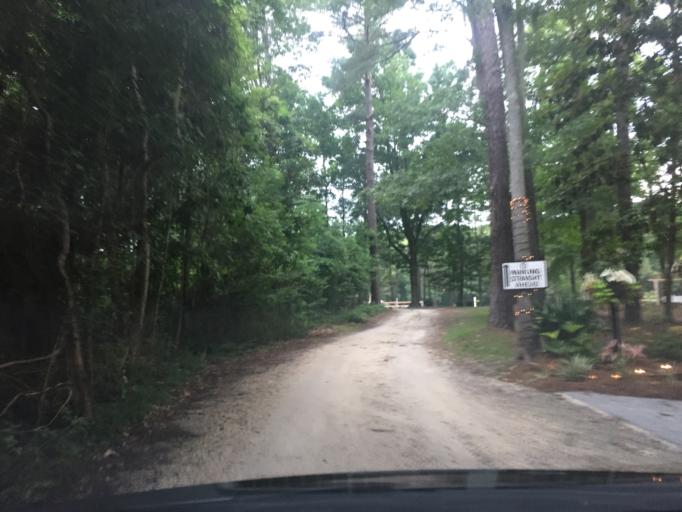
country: US
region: Georgia
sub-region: Chatham County
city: Georgetown
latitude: 32.0374
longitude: -81.1716
